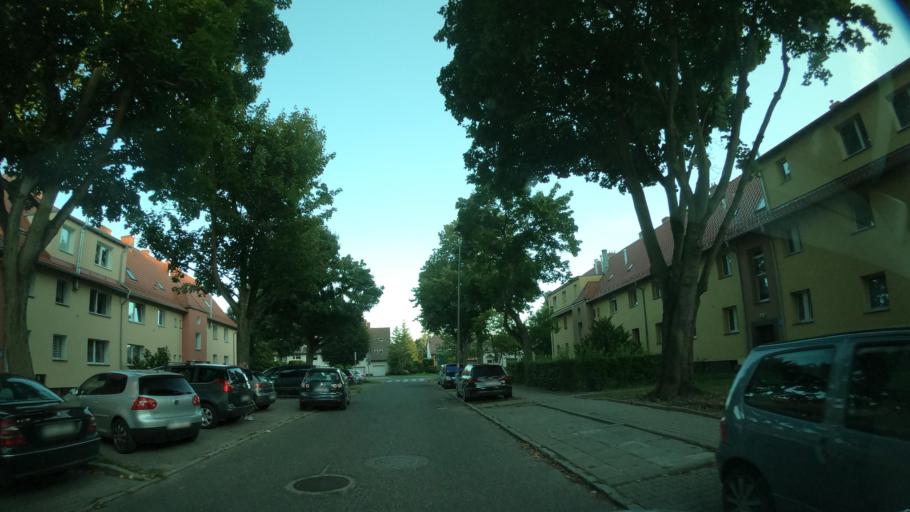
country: PL
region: West Pomeranian Voivodeship
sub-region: Powiat policki
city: Police
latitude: 53.5388
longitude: 14.5551
